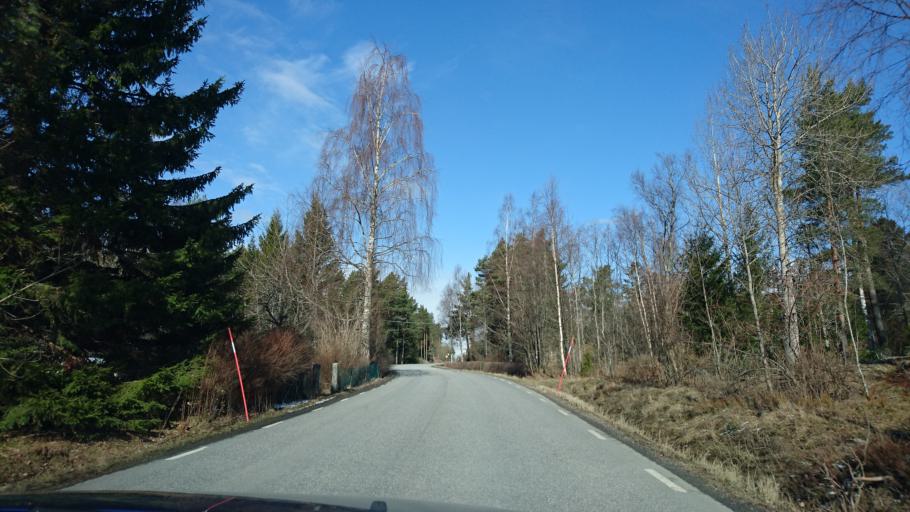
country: SE
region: Stockholm
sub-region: Norrtalje Kommun
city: Bjorko
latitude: 59.8146
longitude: 18.9291
